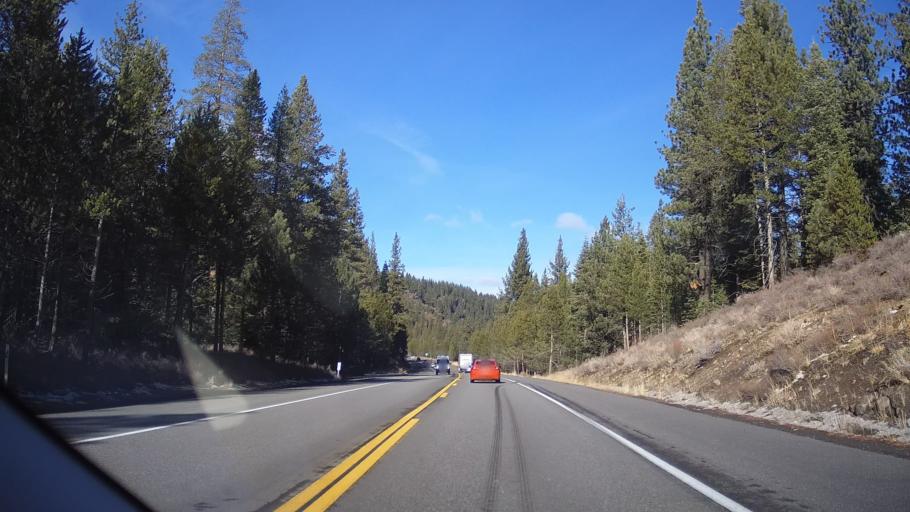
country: US
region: California
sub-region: Nevada County
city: Truckee
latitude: 39.2803
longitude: -120.2069
